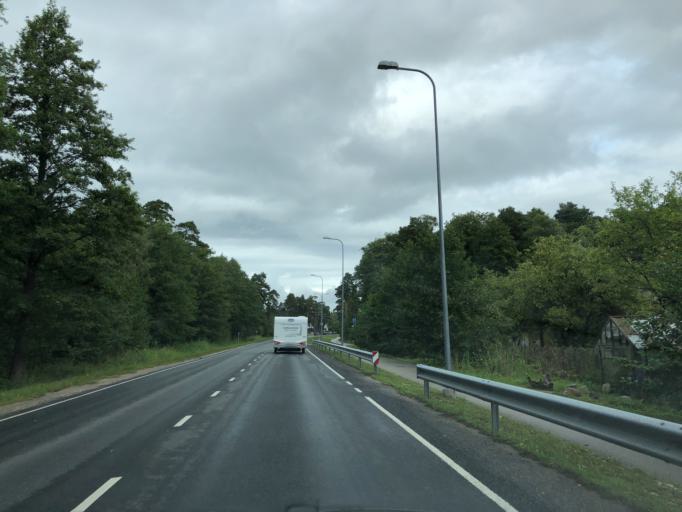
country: EE
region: Laeaene
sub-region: Haapsalu linn
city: Haapsalu
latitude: 58.9266
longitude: 23.5250
